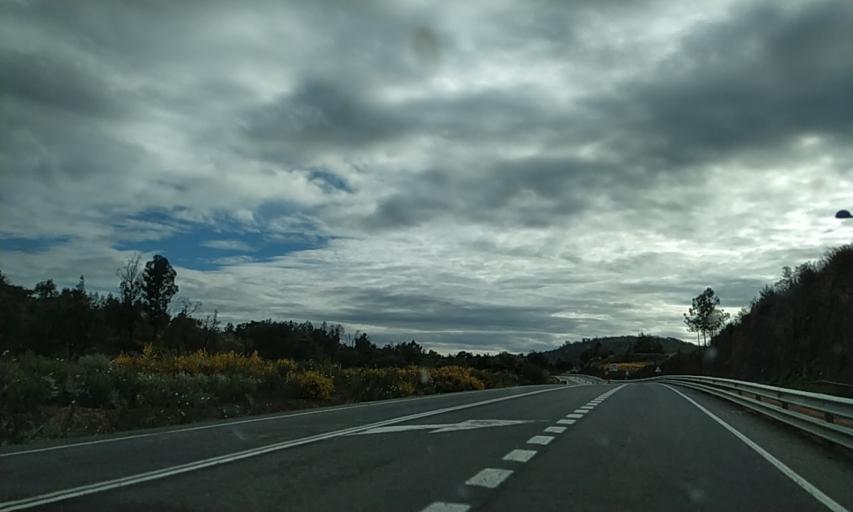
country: ES
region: Extremadura
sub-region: Provincia de Caceres
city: Perales del Puerto
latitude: 40.1651
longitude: -6.6833
